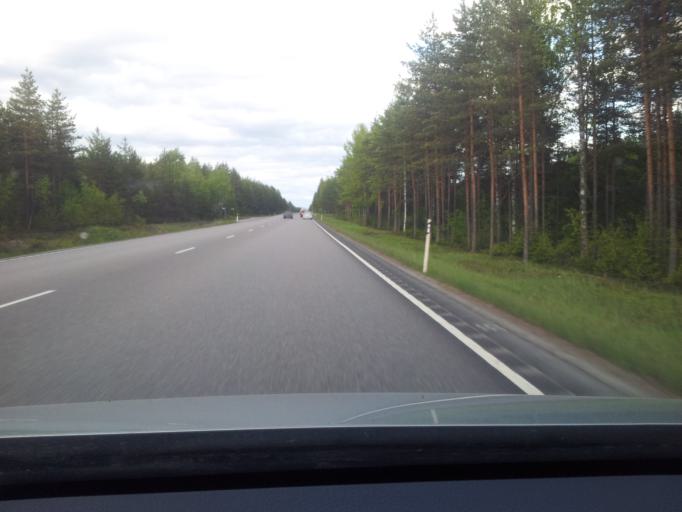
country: FI
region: South Karelia
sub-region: Lappeenranta
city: Taavetti
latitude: 60.9176
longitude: 27.4740
